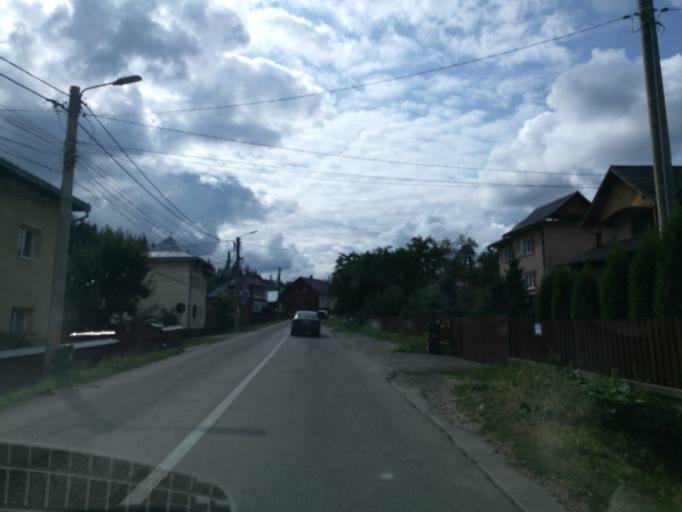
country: RO
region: Suceava
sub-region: Oras Gura Humorului
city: Gura Humorului
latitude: 47.5267
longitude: 25.8641
